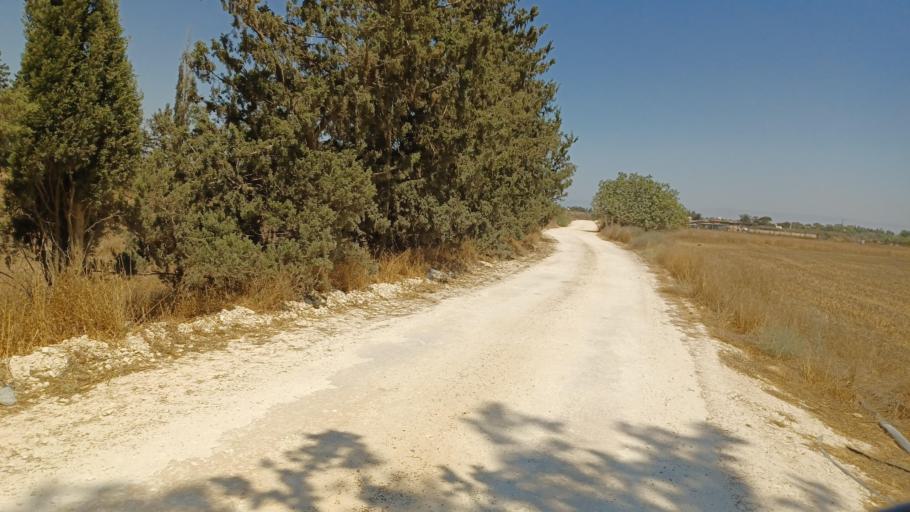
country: CY
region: Ammochostos
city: Acheritou
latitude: 35.0744
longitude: 33.8944
